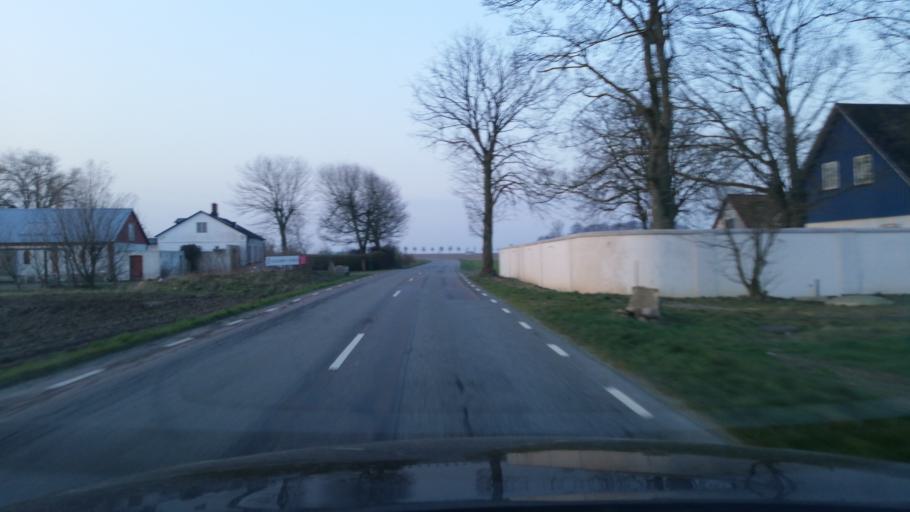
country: SE
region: Skane
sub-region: Tomelilla Kommun
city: Tomelilla
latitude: 55.4721
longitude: 14.0982
